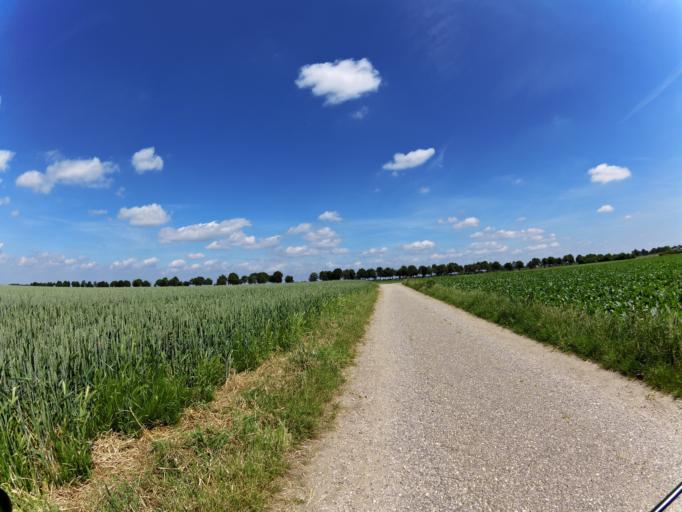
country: NL
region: Limburg
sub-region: Gemeente Sittard-Geleen
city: Sittard
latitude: 51.0170
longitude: 5.8921
